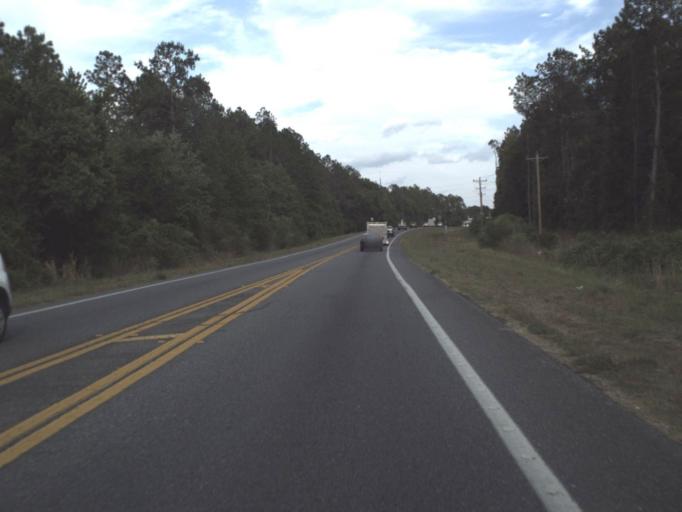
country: US
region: Florida
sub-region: Marion County
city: Silver Springs Shores
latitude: 29.1855
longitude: -81.8973
